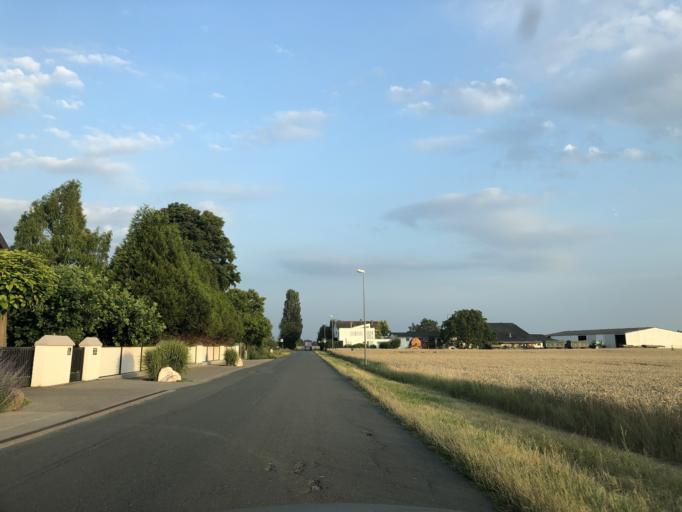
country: DE
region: Rheinland-Pfalz
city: Nierstein
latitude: 49.8892
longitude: 8.3713
